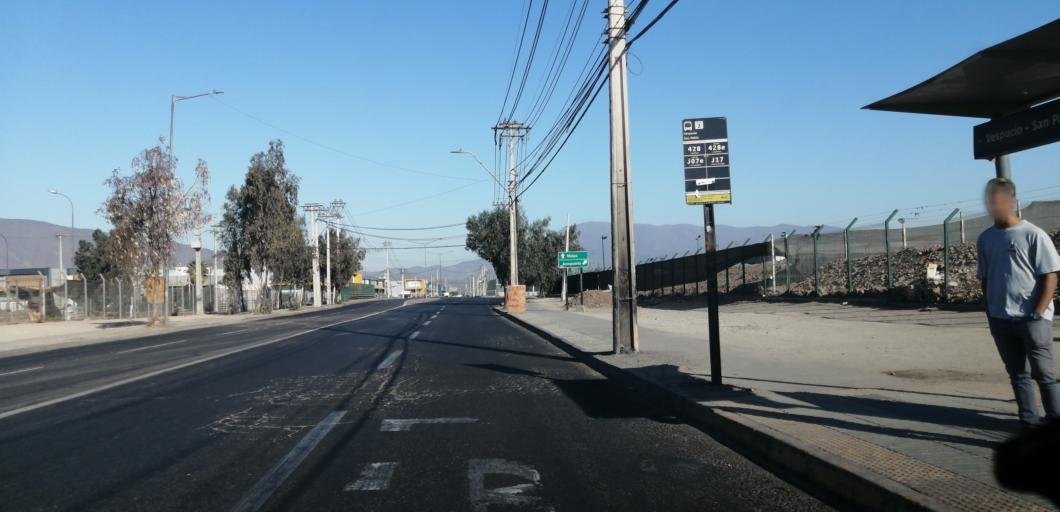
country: CL
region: Santiago Metropolitan
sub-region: Provincia de Santiago
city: Lo Prado
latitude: -33.4441
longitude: -70.7777
